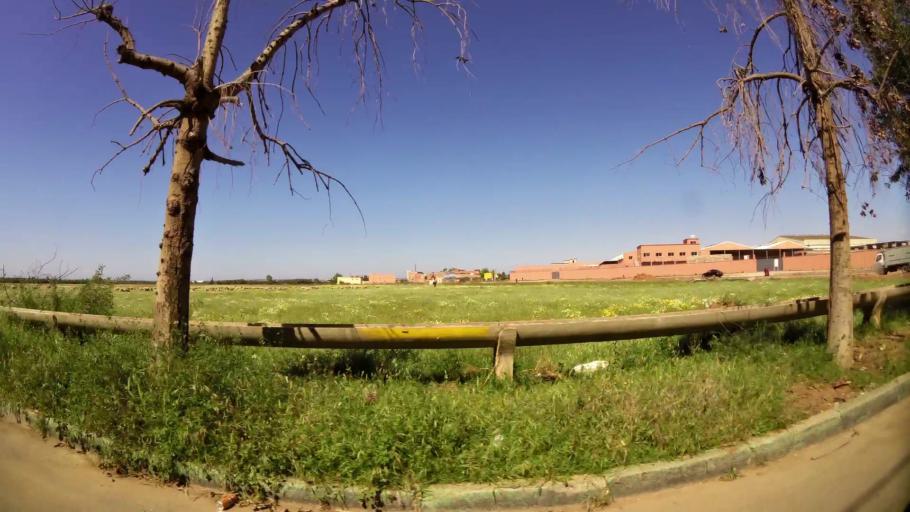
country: MA
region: Oriental
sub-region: Berkane-Taourirt
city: Berkane
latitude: 34.9384
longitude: -2.3222
